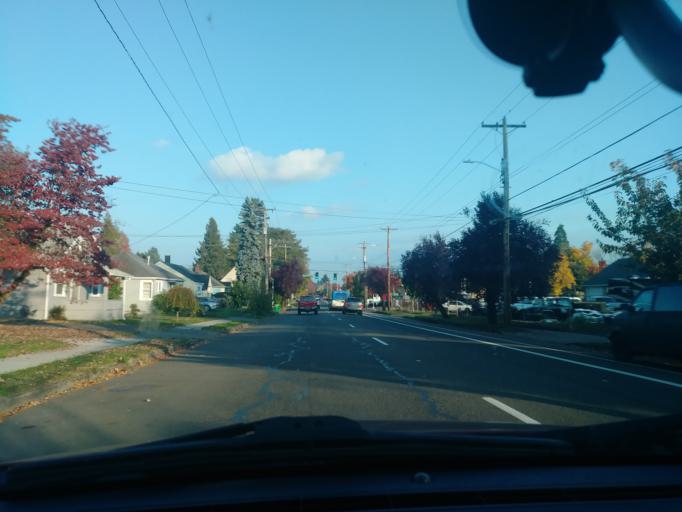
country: US
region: Oregon
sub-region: Washington County
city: Forest Grove
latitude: 45.5183
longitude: -123.1006
